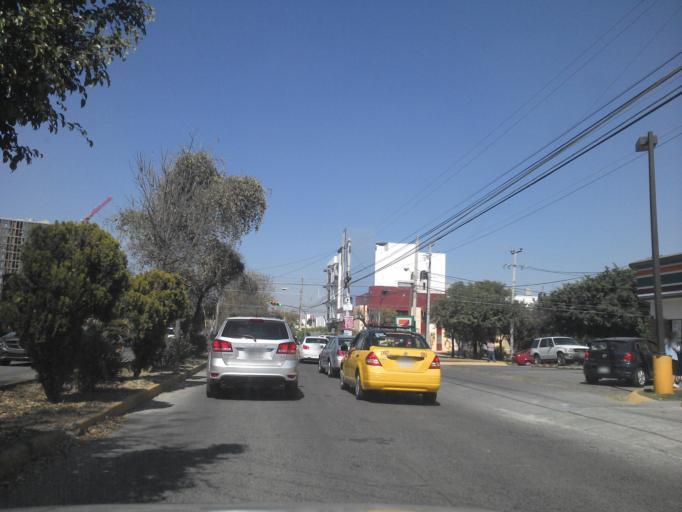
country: MX
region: Jalisco
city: Guadalajara
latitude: 20.6871
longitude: -103.3933
